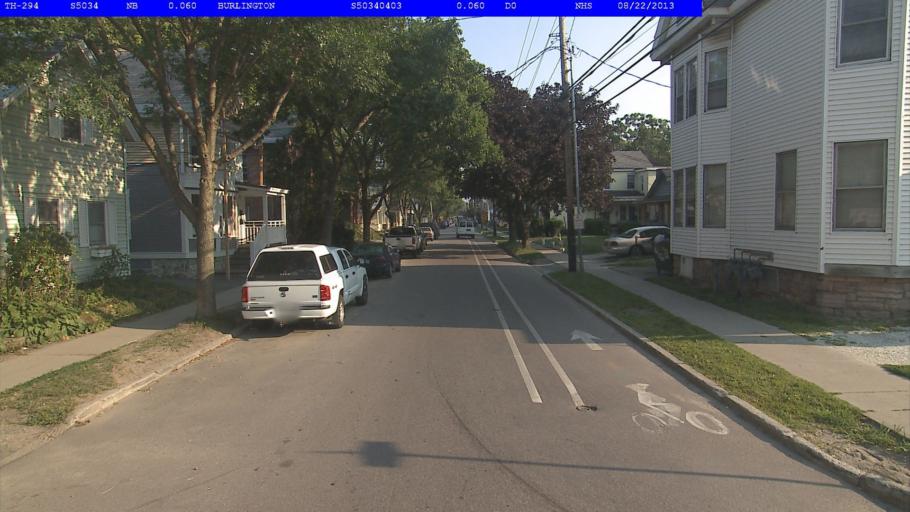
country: US
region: Vermont
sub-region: Chittenden County
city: Burlington
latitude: 44.4814
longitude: -73.2094
